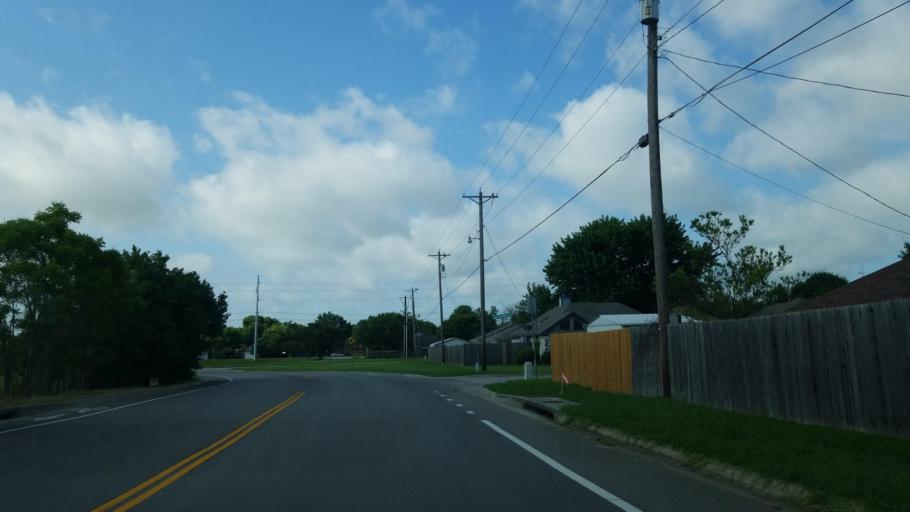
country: US
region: Texas
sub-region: Denton County
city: Denton
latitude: 33.2231
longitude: -97.0978
